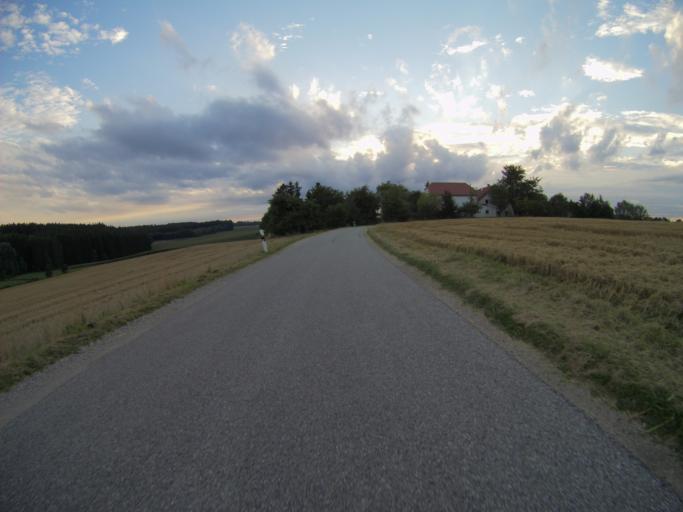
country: DE
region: Bavaria
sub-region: Upper Bavaria
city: Wolfersdorf
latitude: 48.4354
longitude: 11.7061
